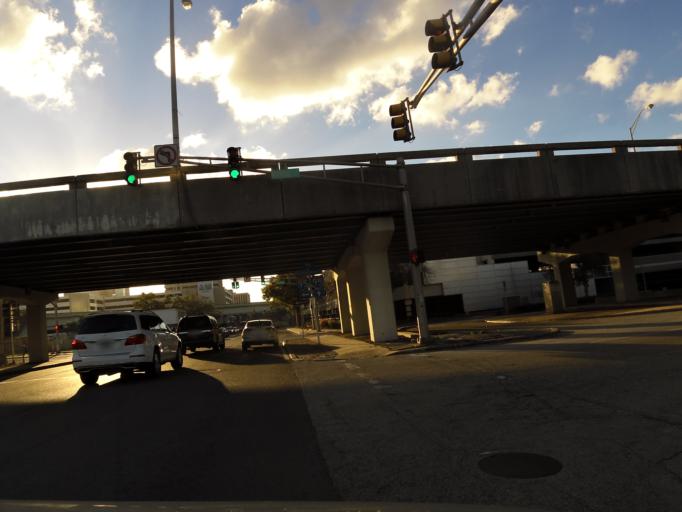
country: US
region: Florida
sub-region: Duval County
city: Jacksonville
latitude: 30.2920
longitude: -81.6572
